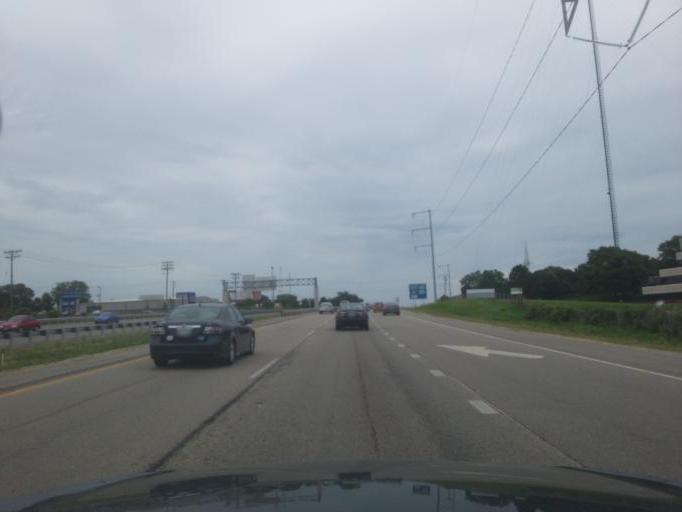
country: US
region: Wisconsin
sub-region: Dane County
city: Middleton
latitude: 43.0529
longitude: -89.4914
